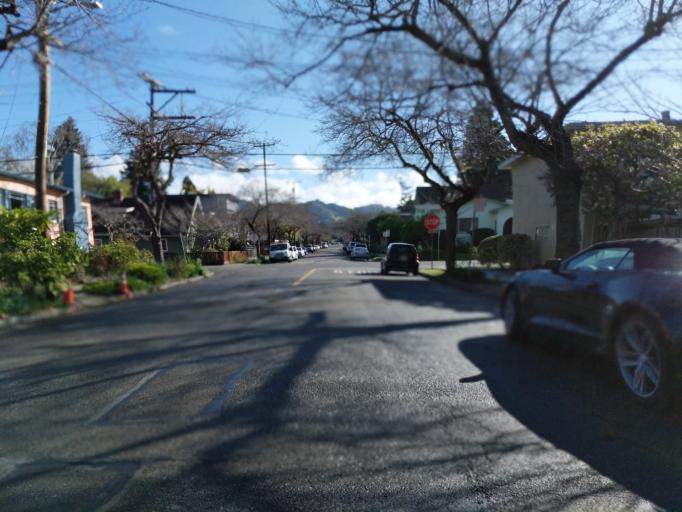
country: US
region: California
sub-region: Alameda County
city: Berkeley
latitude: 37.8619
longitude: -122.2768
